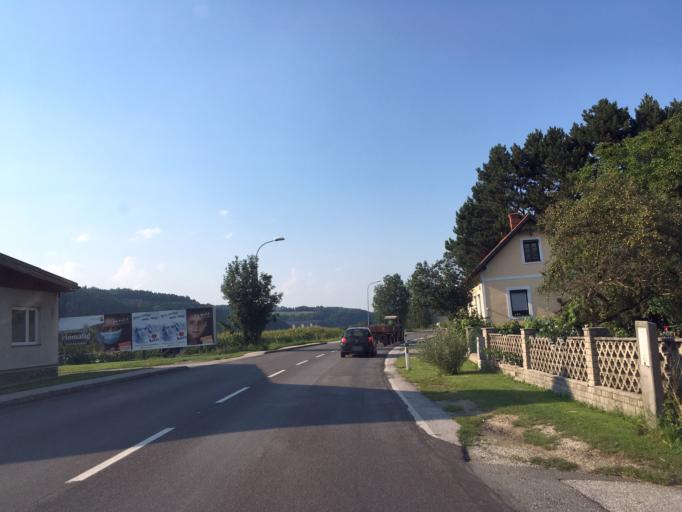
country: AT
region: Lower Austria
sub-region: Politischer Bezirk Neunkirchen
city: Warth
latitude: 47.6381
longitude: 16.1297
